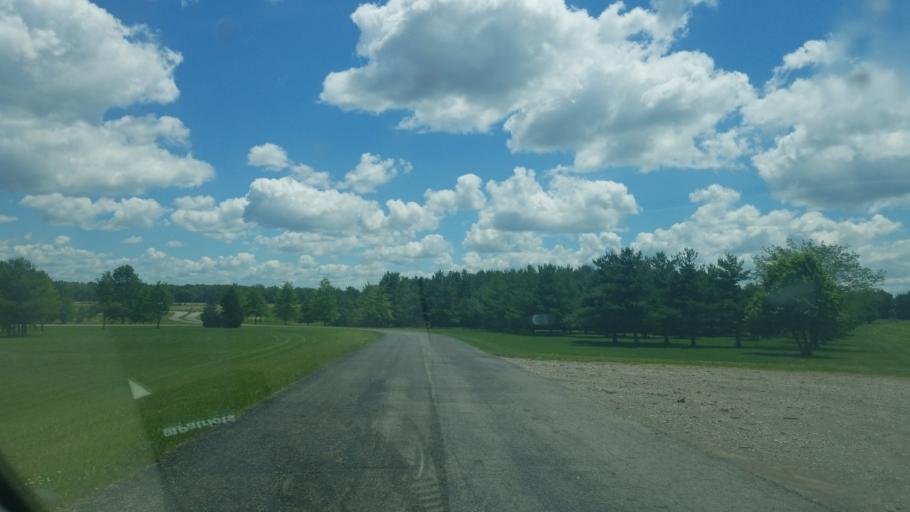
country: US
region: Ohio
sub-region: Huron County
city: New London
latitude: 41.0703
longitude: -82.4210
